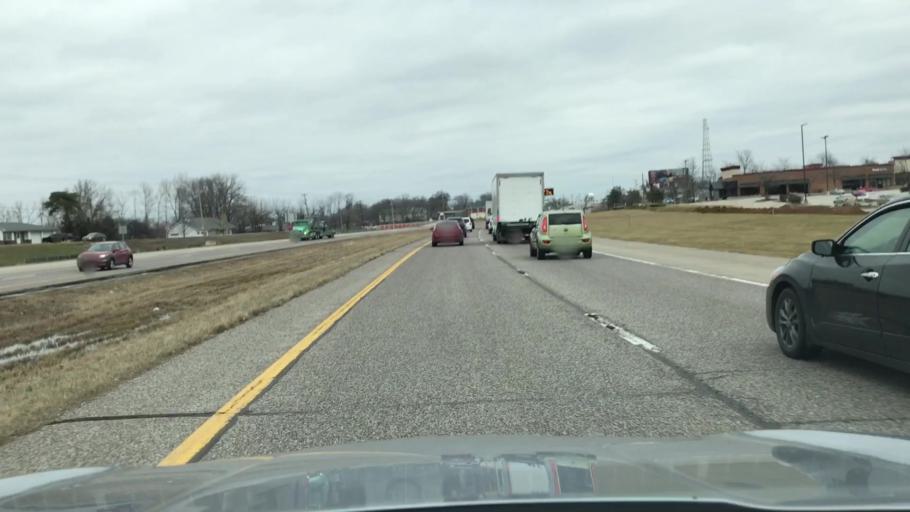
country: US
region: Missouri
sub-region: Saint Charles County
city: Saint Charles
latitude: 38.7698
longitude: -90.5227
